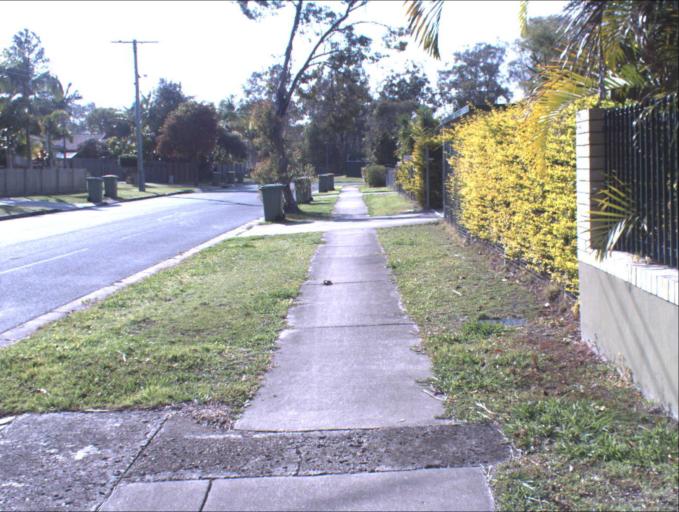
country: AU
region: Queensland
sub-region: Logan
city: Waterford West
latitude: -27.6873
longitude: 153.1253
